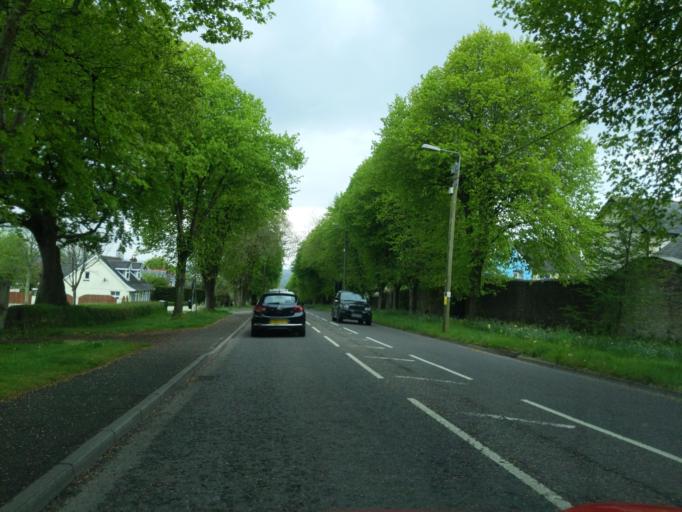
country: GB
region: England
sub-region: Cornwall
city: Bodmin
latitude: 50.4685
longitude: -4.7367
